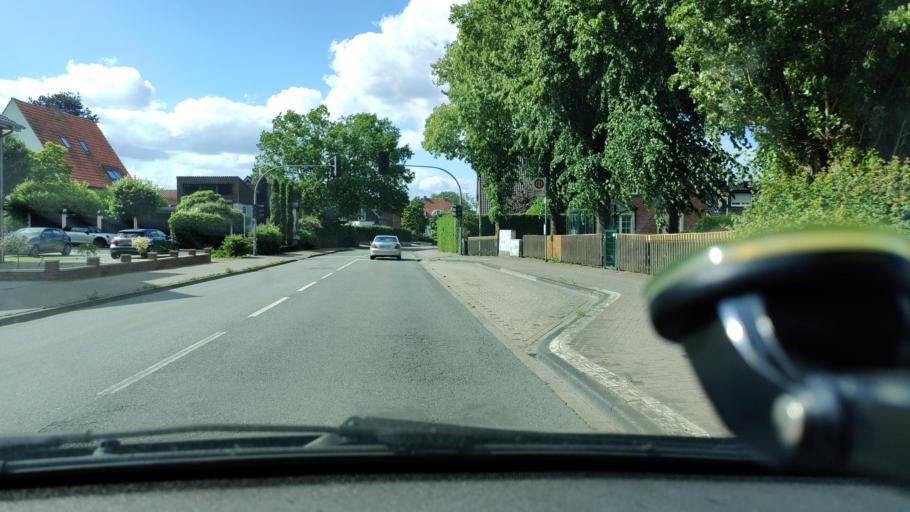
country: DE
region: North Rhine-Westphalia
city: Stadtlohn
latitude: 51.9934
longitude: 6.9279
